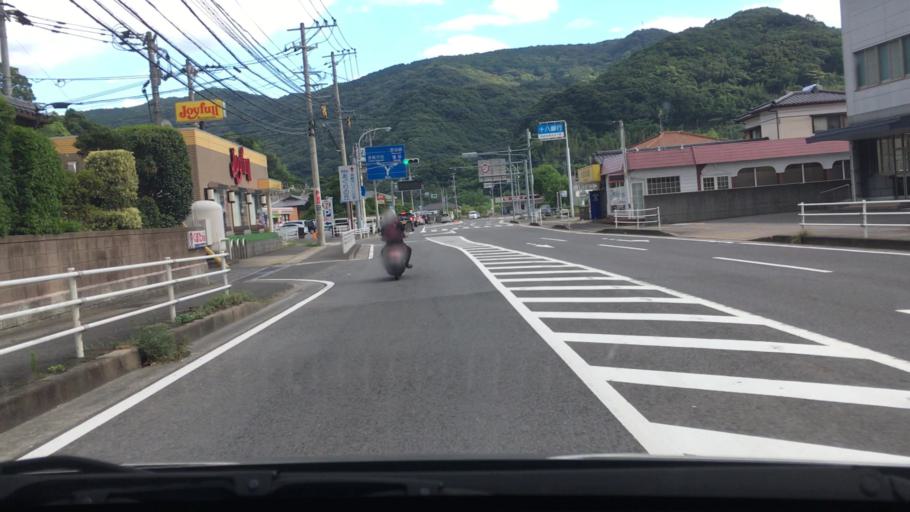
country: JP
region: Nagasaki
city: Togitsu
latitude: 32.8281
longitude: 129.7838
